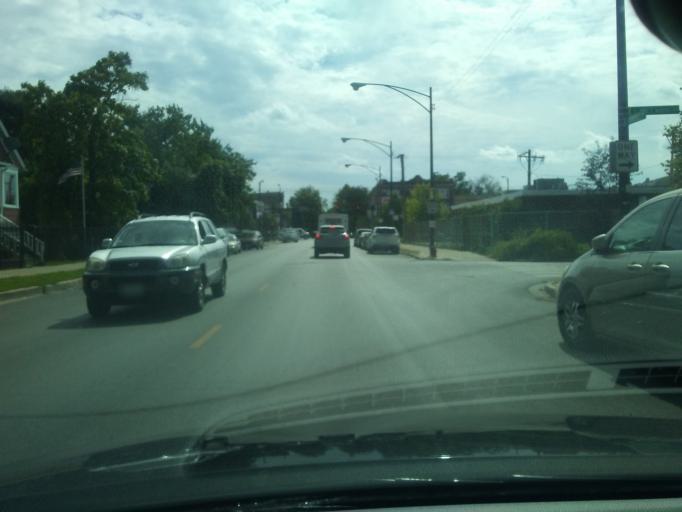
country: US
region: Illinois
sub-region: Cook County
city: Oak Park
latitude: 41.9184
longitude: -87.7119
